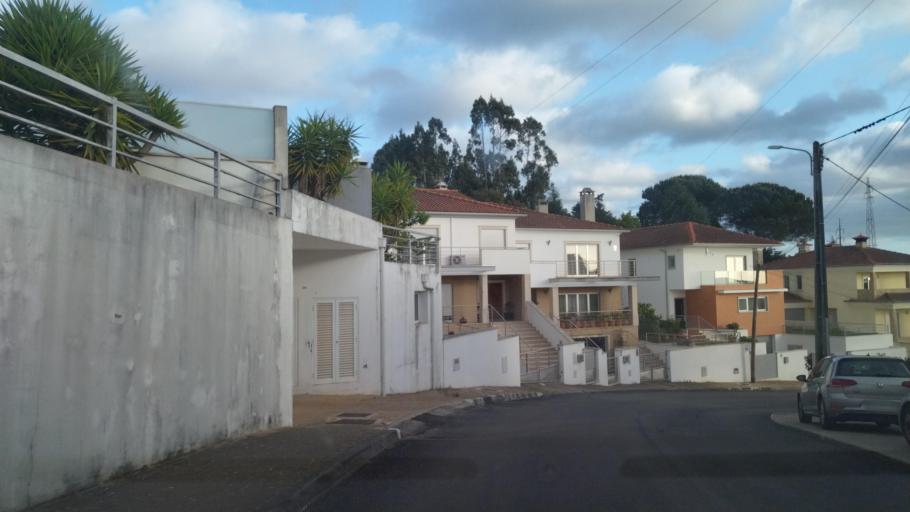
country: PT
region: Coimbra
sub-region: Coimbra
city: Coimbra
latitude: 40.1694
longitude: -8.4417
